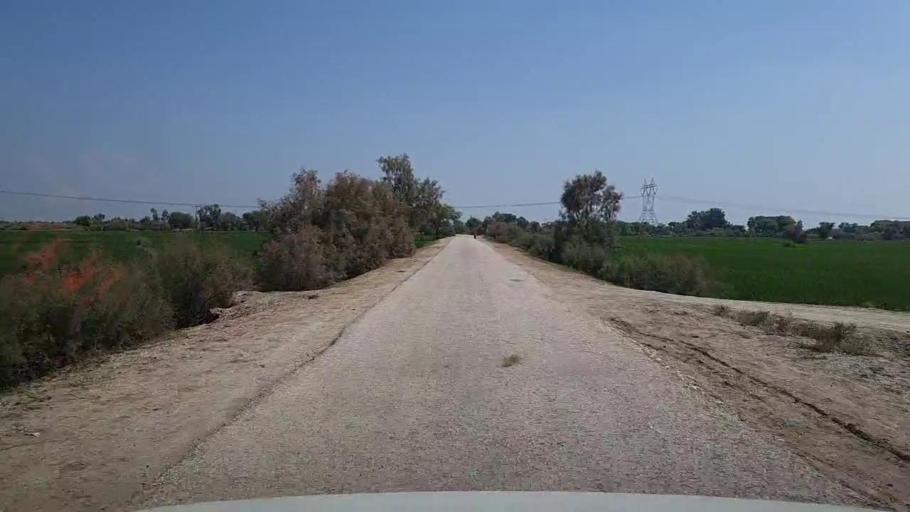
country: PK
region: Sindh
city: Kandhkot
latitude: 28.3076
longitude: 69.3423
